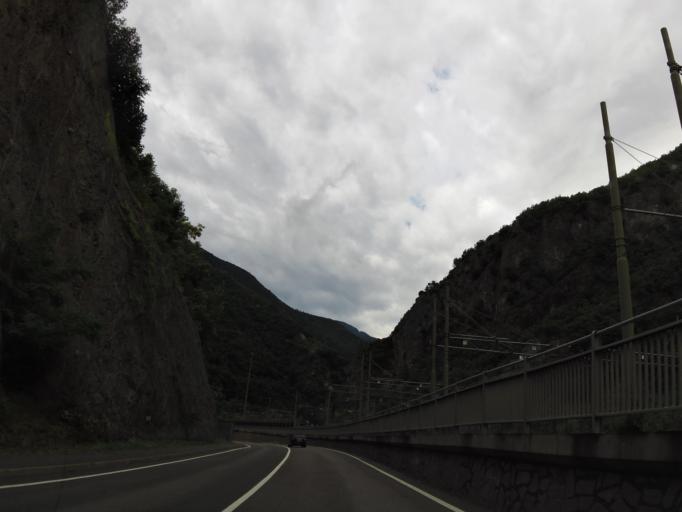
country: IT
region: Trentino-Alto Adige
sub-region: Bolzano
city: Cornedo All'Isarco
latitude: 46.4954
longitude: 11.4427
